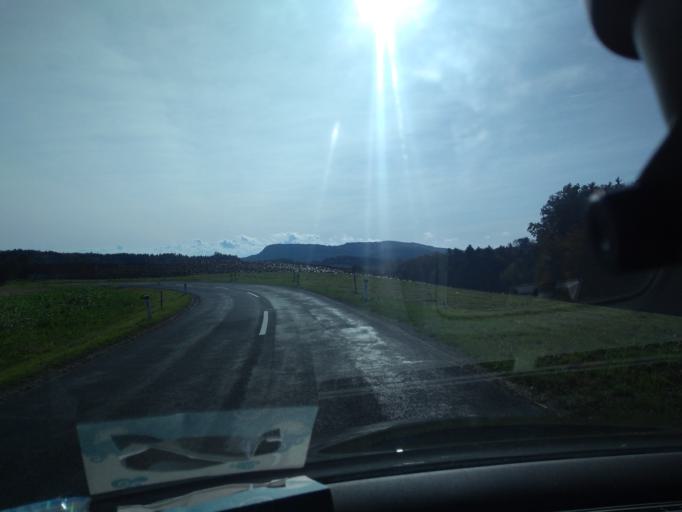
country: AT
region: Styria
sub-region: Politischer Bezirk Leibnitz
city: Sankt Ulrich am Waasen
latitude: 46.9175
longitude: 15.5308
